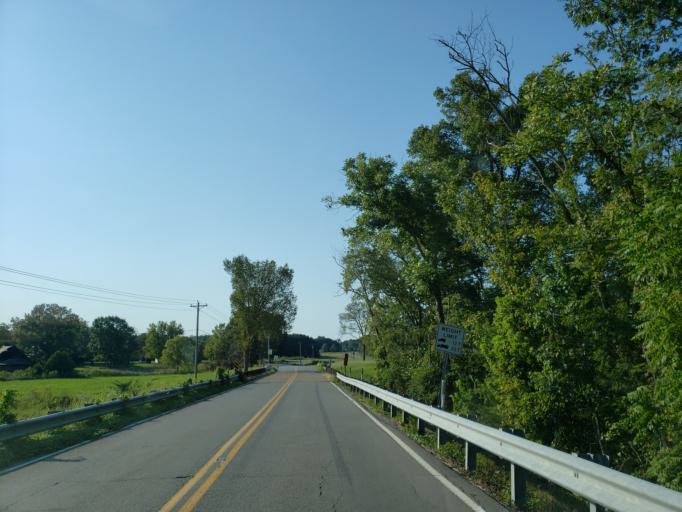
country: US
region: Tennessee
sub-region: Bradley County
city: Wildwood Lake
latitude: 35.0467
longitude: -84.7467
